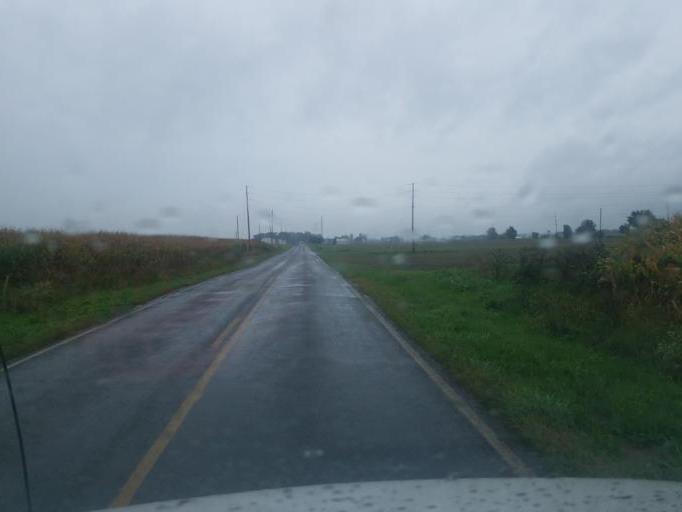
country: US
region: Ohio
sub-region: Medina County
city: Seville
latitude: 41.0053
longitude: -81.8603
